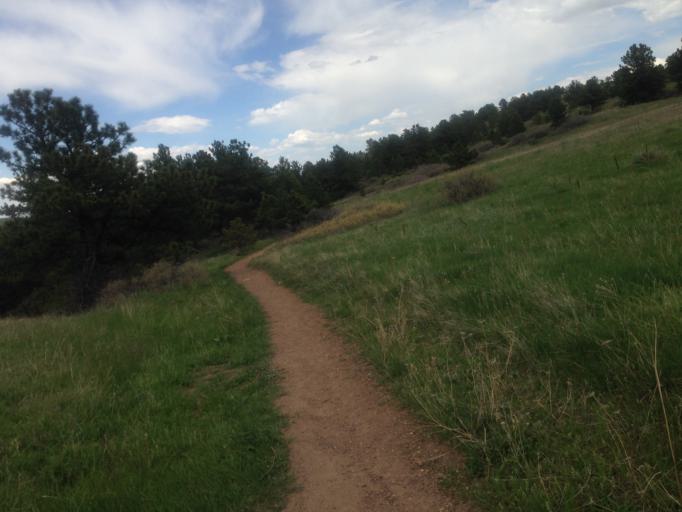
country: US
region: Colorado
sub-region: Boulder County
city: Superior
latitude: 39.9508
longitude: -105.2229
